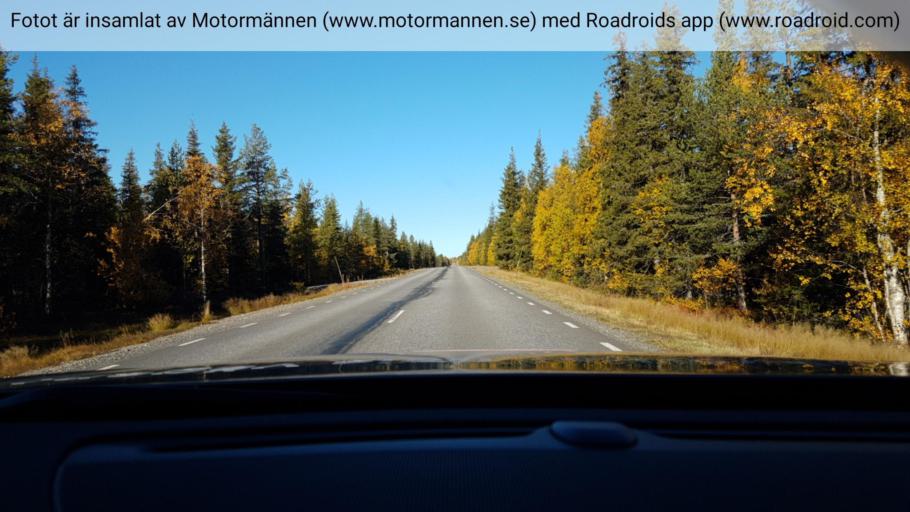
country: SE
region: Vaesterbotten
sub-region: Skelleftea Kommun
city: Storvik
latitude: 65.3553
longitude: 20.4709
